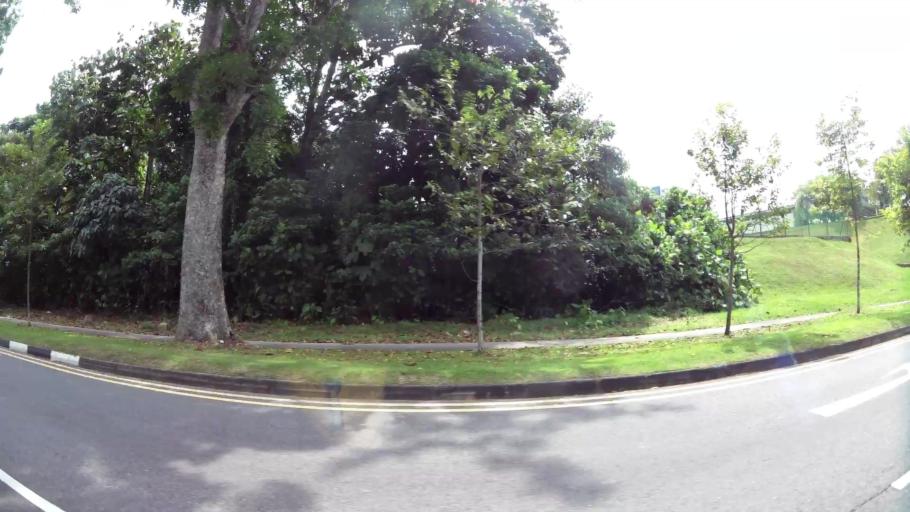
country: MY
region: Johor
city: Johor Bahru
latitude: 1.4109
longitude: 103.7620
